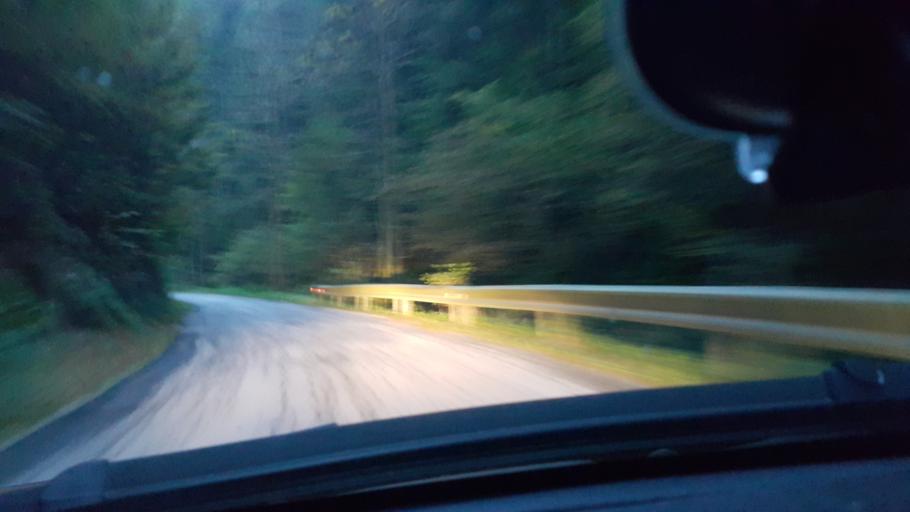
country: SI
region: Vitanje
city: Vitanje
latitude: 46.4016
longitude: 15.2992
